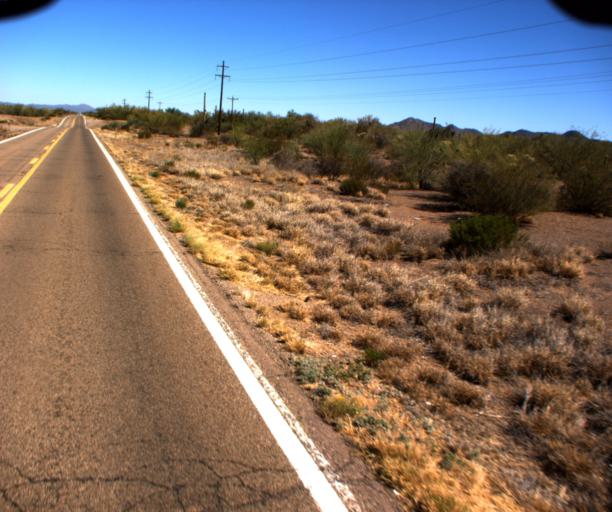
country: US
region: Arizona
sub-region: Pima County
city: Sells
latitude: 31.9917
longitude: -111.9786
